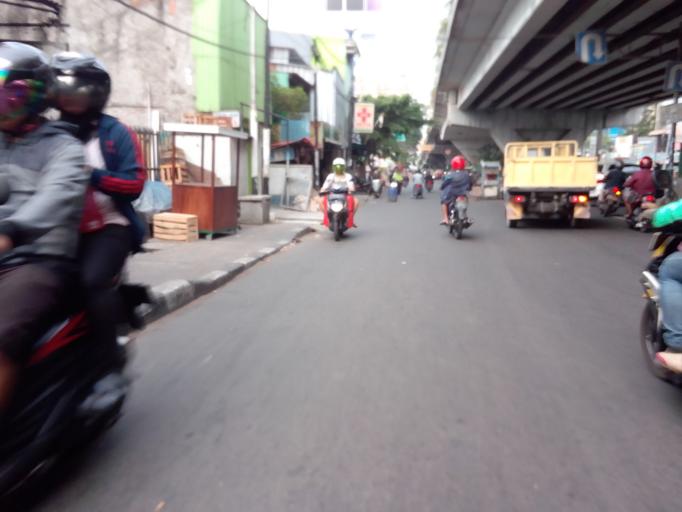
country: ID
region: Jakarta Raya
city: Jakarta
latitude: -6.1660
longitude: 106.8010
